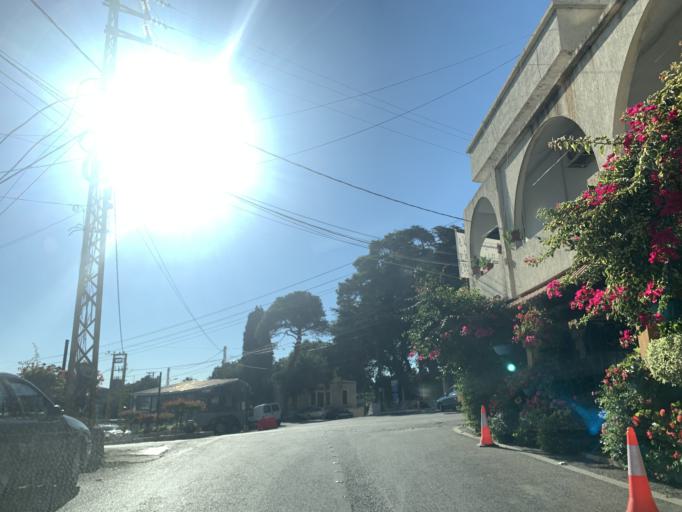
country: LB
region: Mont-Liban
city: Djounie
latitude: 33.9817
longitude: 35.6562
